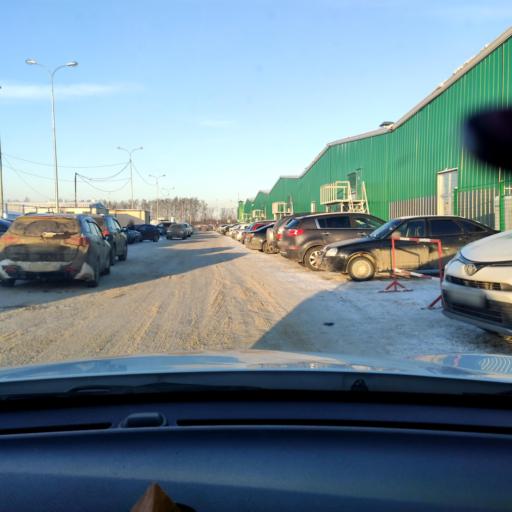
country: RU
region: Tatarstan
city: Osinovo
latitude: 55.8565
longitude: 48.8332
